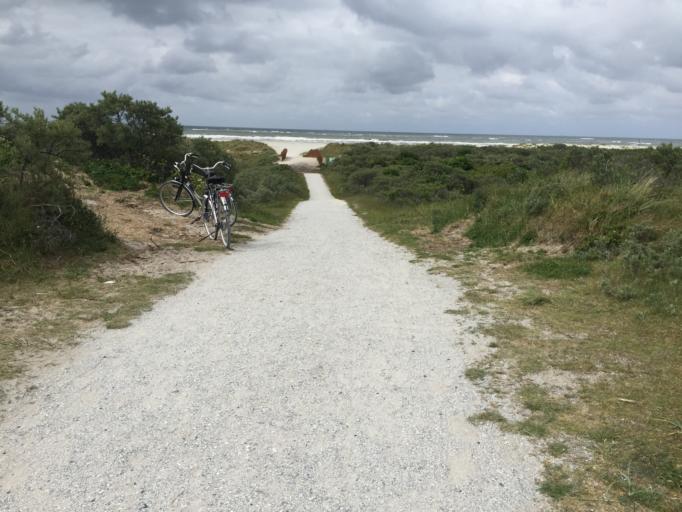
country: NL
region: Friesland
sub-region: Gemeente Schiermonnikoog
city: Schiermonnikoog
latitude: 53.4965
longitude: 6.1650
